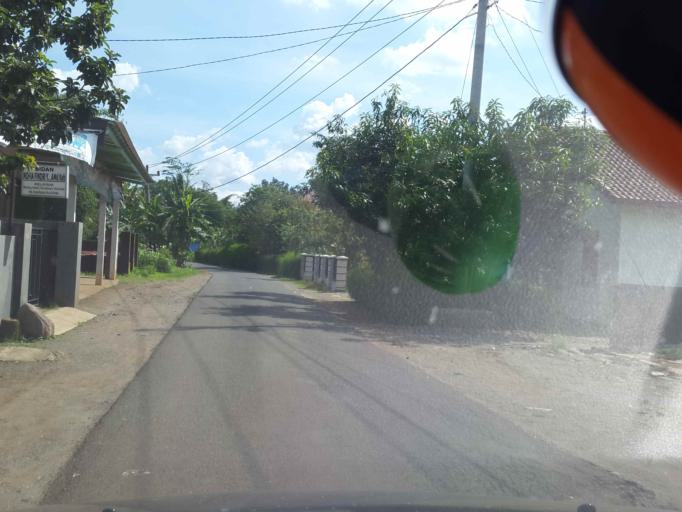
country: ID
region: Central Java
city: Gombong
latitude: -7.4550
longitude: 109.6016
